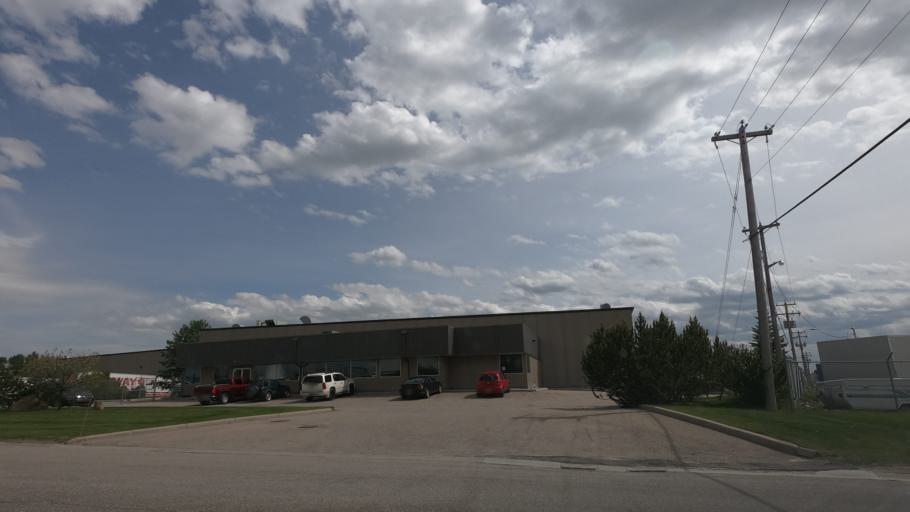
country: CA
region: Alberta
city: Airdrie
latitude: 51.2913
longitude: -113.9854
